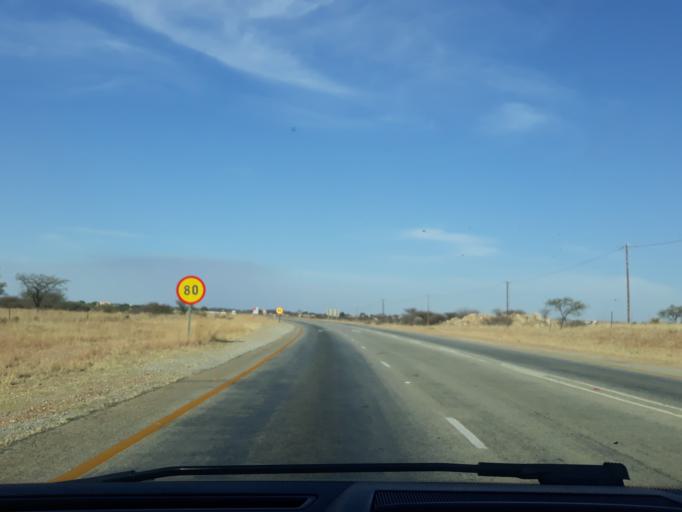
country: ZA
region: Limpopo
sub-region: Capricorn District Municipality
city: Polokwane
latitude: -23.9472
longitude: 29.4097
